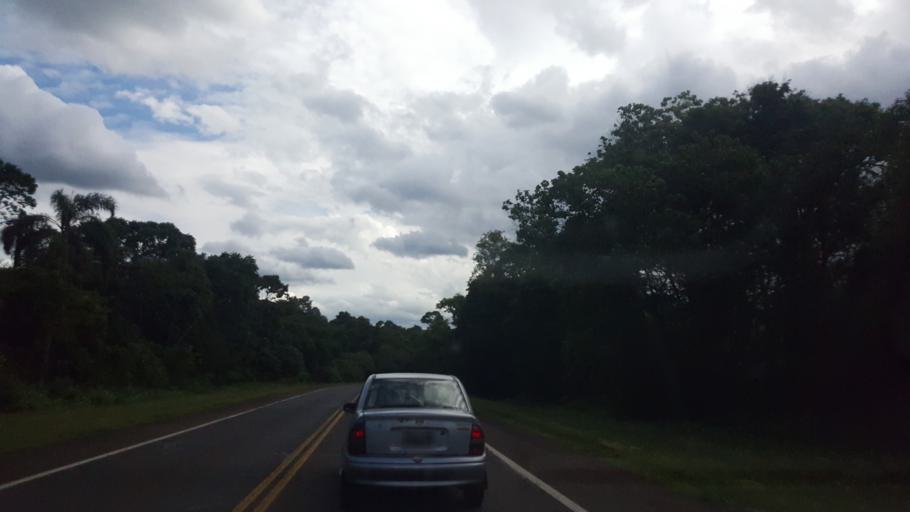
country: AR
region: Misiones
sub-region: Departamento de Iguazu
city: Puerto Iguazu
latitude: -25.7161
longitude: -54.5198
